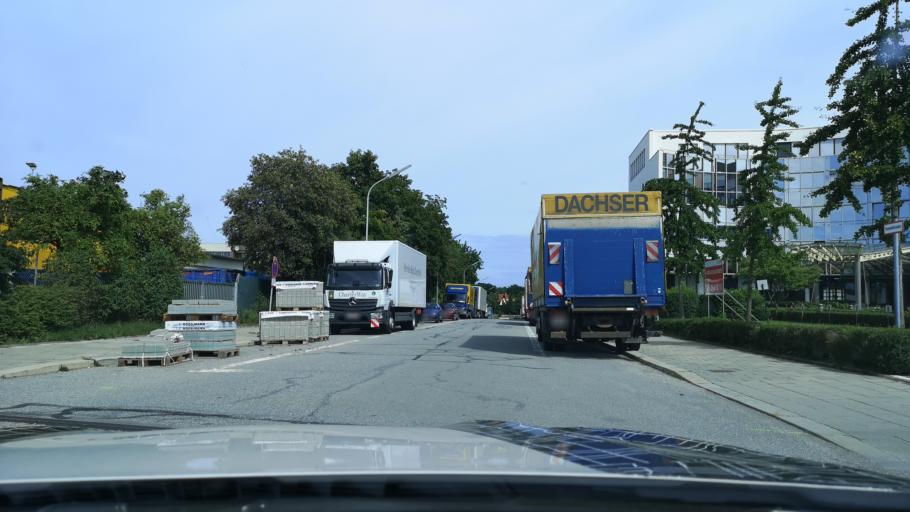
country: DE
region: Bavaria
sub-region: Upper Bavaria
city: Bogenhausen
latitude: 48.1367
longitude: 11.6397
